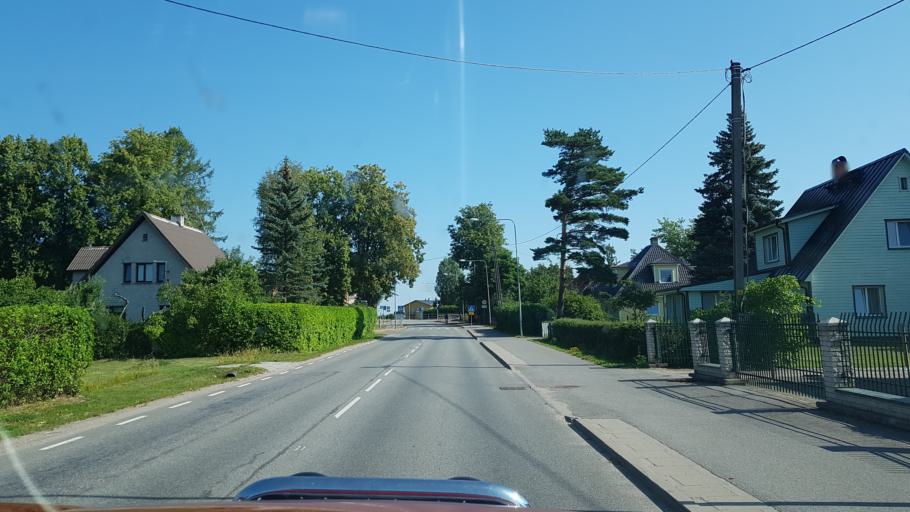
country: EE
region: Tartu
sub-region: Tartu linn
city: Tartu
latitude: 58.4227
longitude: 26.7630
